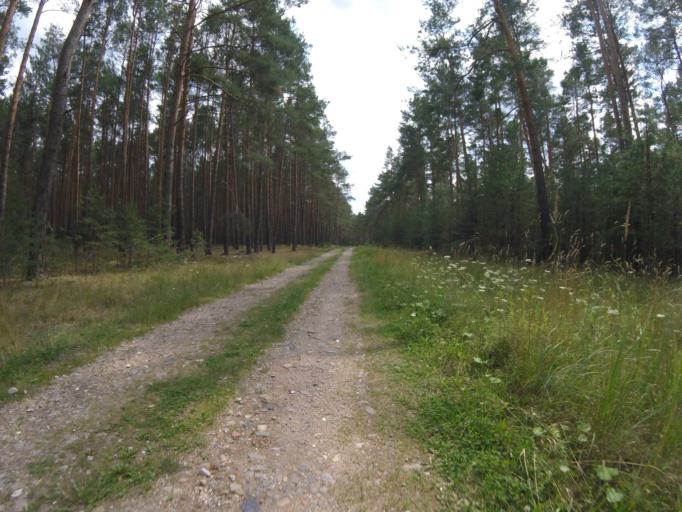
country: DE
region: Brandenburg
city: Halbe
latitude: 52.1247
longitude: 13.6968
